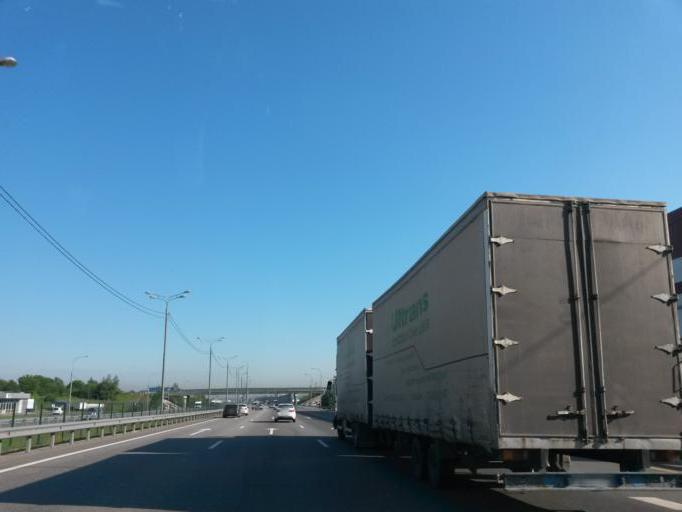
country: RU
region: Moskovskaya
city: Yam
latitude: 55.4731
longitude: 37.7505
